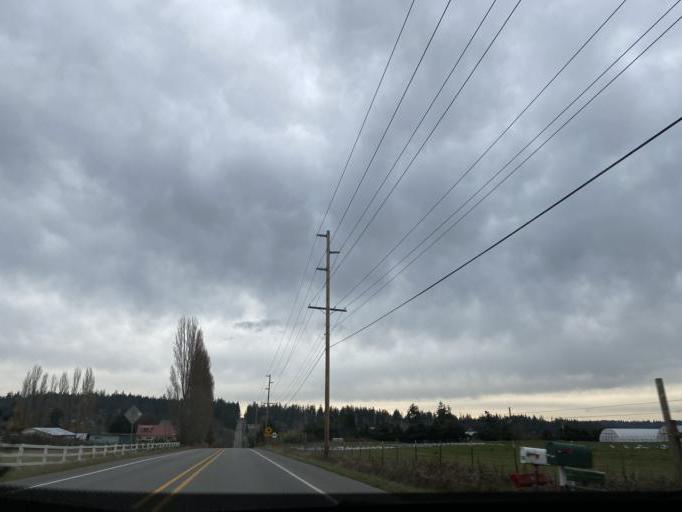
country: US
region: Washington
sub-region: Island County
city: Freeland
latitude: 48.0143
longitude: -122.5749
